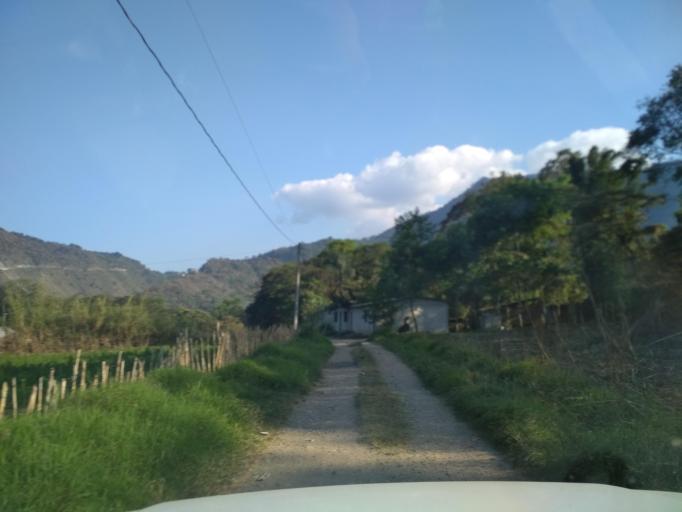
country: MX
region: Veracruz
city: Jalapilla
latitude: 18.8171
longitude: -97.0742
